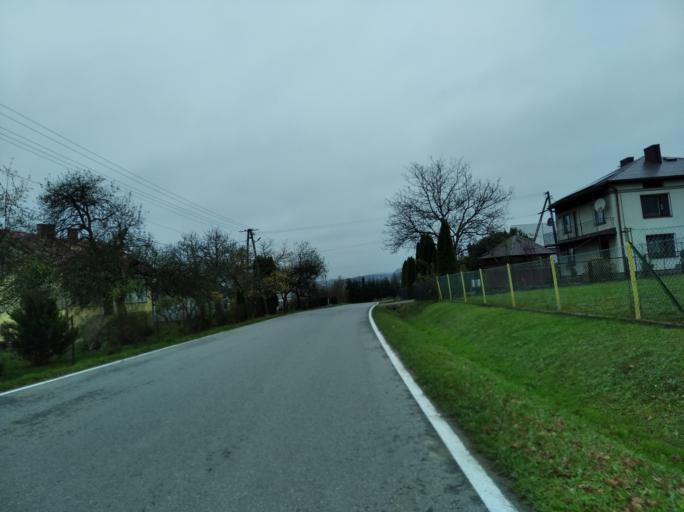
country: PL
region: Subcarpathian Voivodeship
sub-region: Powiat krosnienski
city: Leki
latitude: 49.8242
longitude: 21.6421
